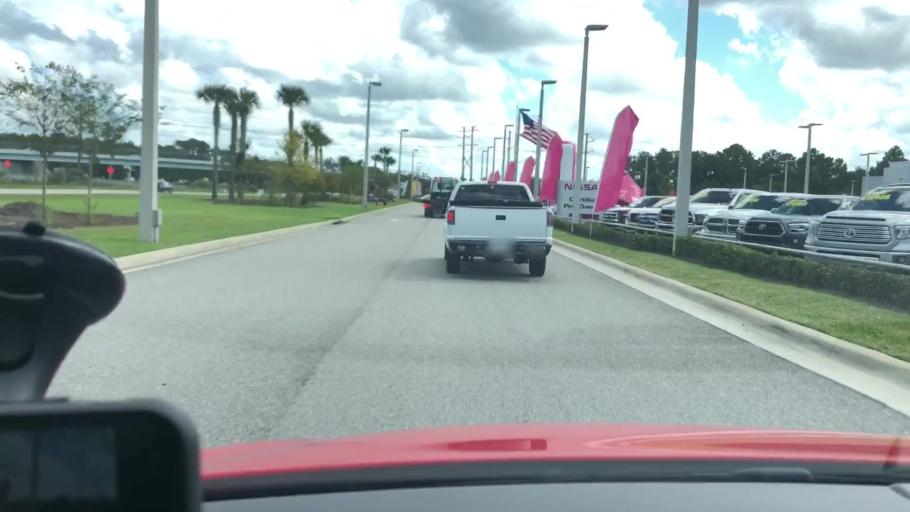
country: US
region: Florida
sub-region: Volusia County
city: Holly Hill
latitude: 29.2002
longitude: -81.0973
